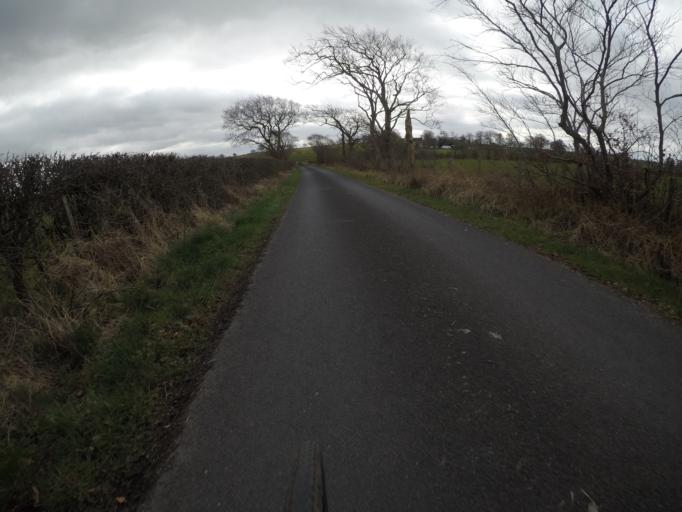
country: GB
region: Scotland
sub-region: North Ayrshire
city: Springside
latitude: 55.6649
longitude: -4.5913
